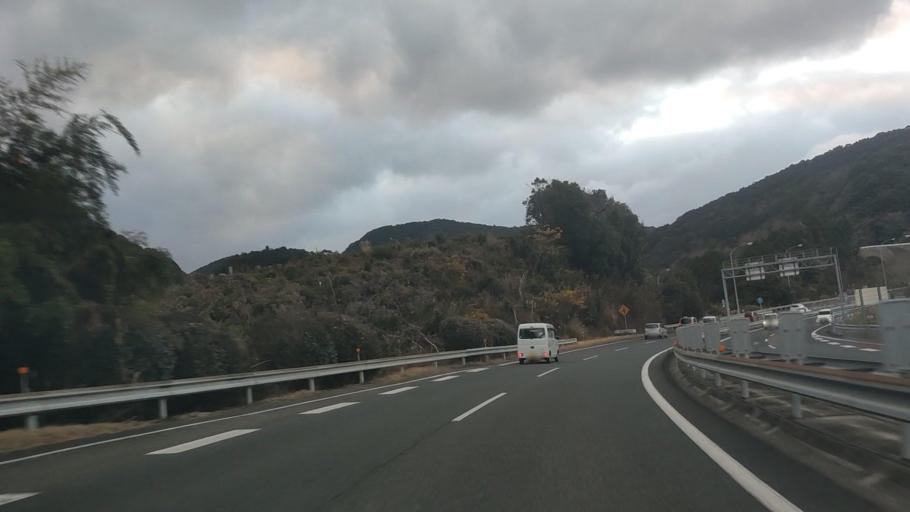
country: JP
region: Nagasaki
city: Obita
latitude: 32.8119
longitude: 129.9582
